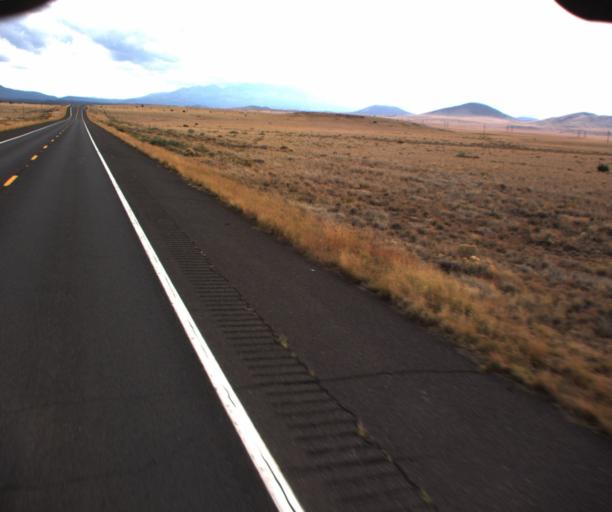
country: US
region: Arizona
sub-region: Coconino County
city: Flagstaff
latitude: 35.5858
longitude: -111.5287
